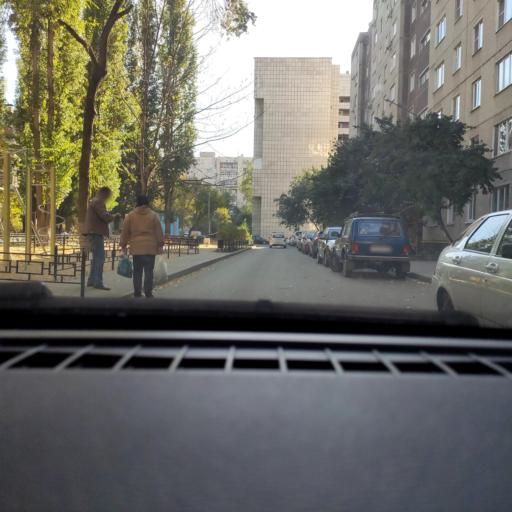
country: RU
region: Voronezj
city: Voronezh
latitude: 51.6706
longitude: 39.2454
